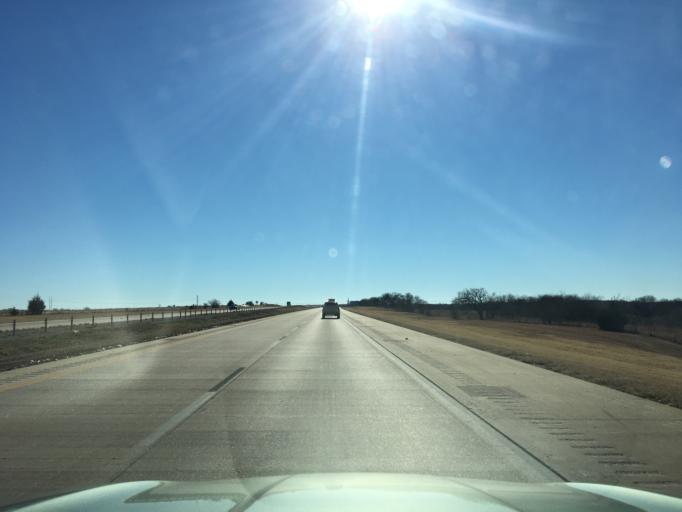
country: US
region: Oklahoma
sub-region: Noble County
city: Perry
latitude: 36.4336
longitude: -97.3271
